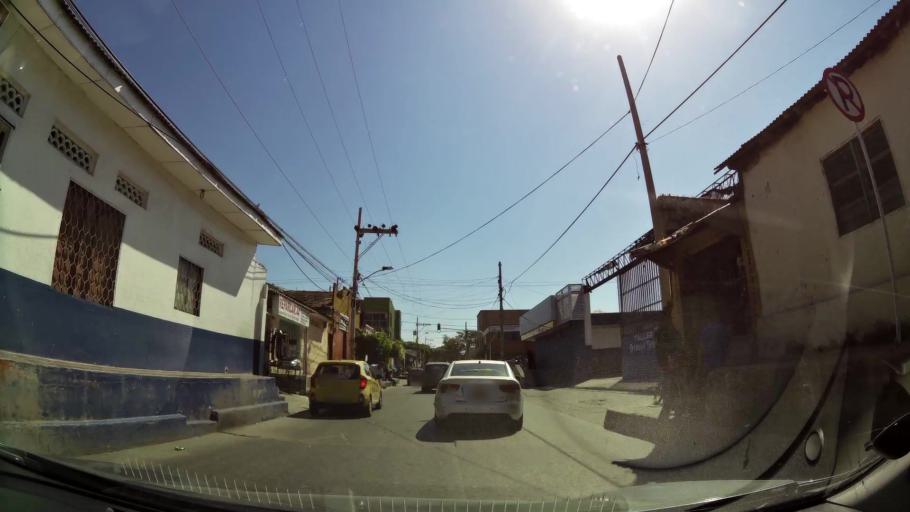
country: CO
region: Atlantico
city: Barranquilla
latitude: 10.9800
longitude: -74.7860
